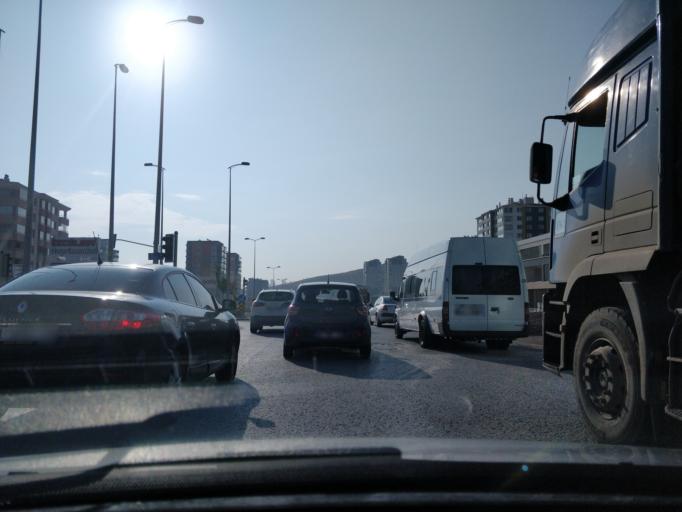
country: TR
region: Ankara
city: Etimesgut
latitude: 39.8973
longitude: 32.6518
